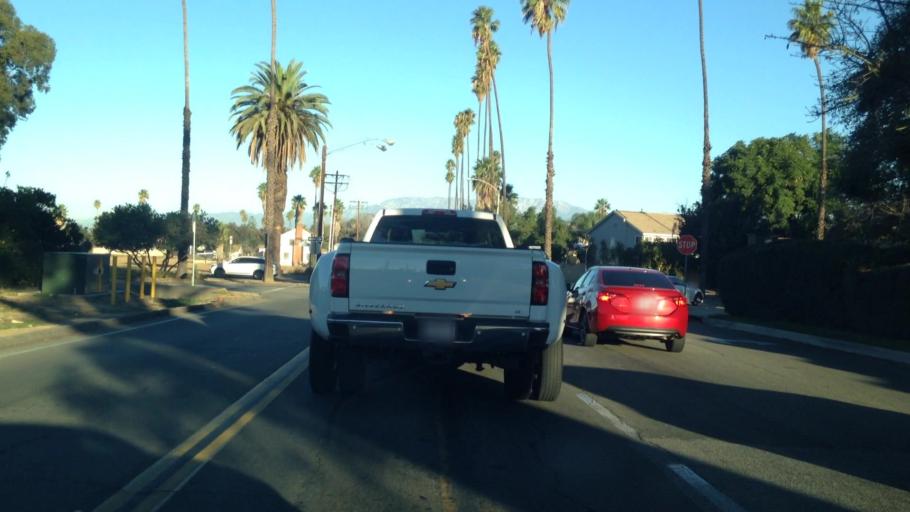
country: US
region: California
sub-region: Riverside County
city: Riverside
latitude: 33.9296
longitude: -117.3889
